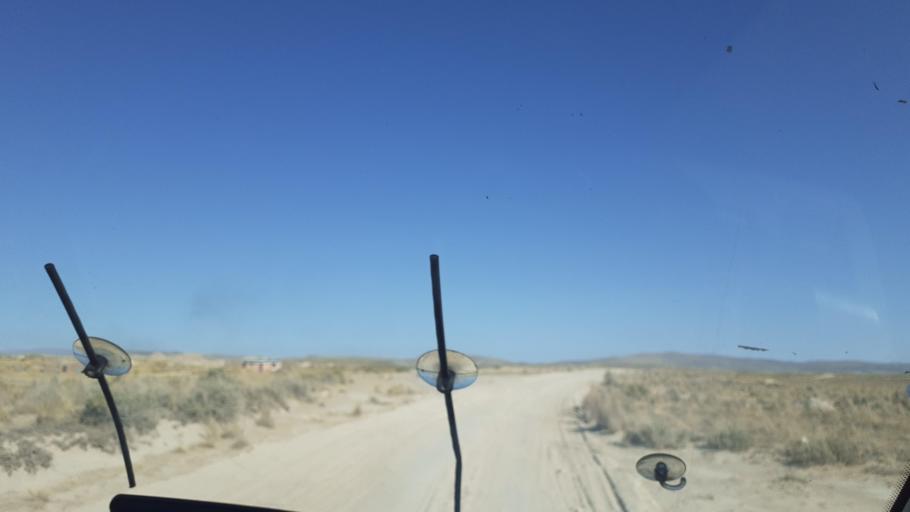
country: BO
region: La Paz
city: Tiahuanaco
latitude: -17.1154
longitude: -68.7976
